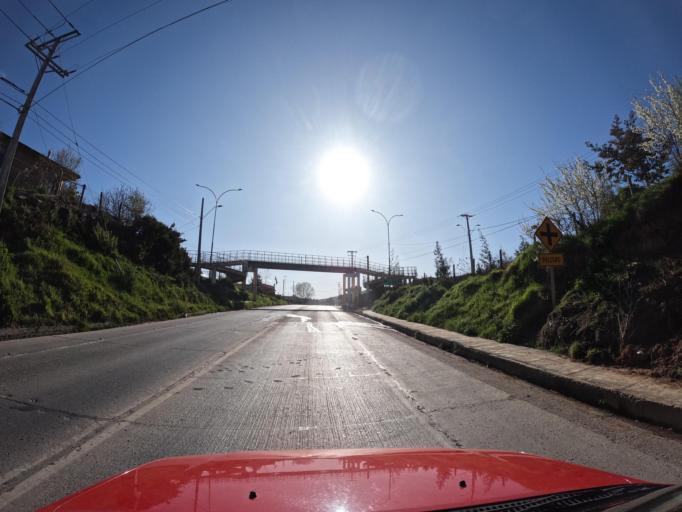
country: CL
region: Maule
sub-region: Provincia de Talca
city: Constitucion
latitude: -35.4514
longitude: -72.2785
